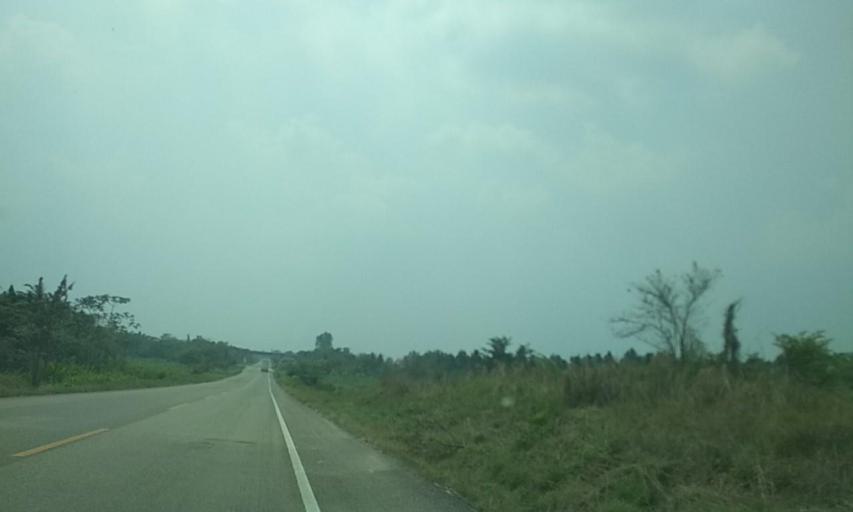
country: MX
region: Tabasco
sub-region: Huimanguillo
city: Francisco Rueda
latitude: 17.7549
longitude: -94.0009
